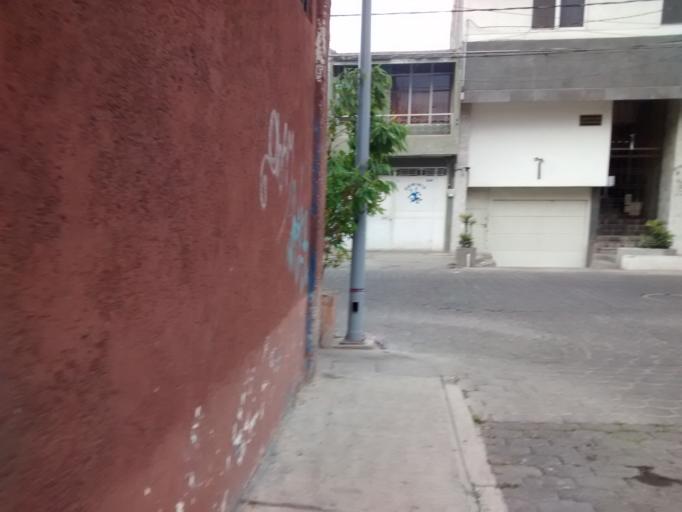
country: MX
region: Puebla
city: Tehuacan
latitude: 18.4696
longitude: -97.3915
